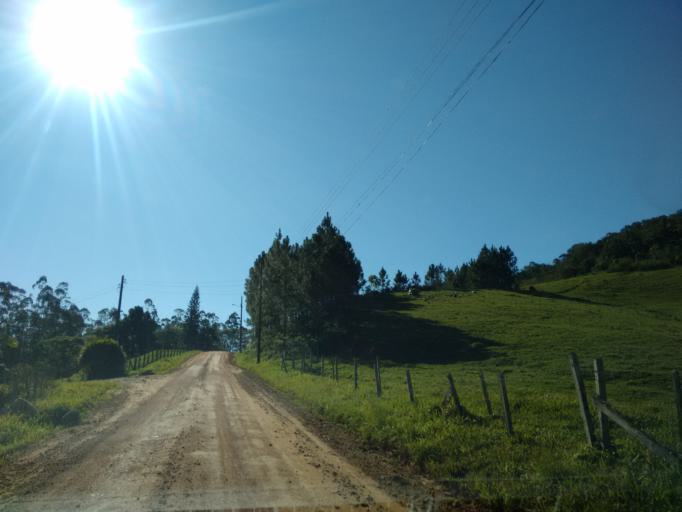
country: BR
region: Santa Catarina
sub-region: Pomerode
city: Pomerode
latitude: -26.6946
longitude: -49.1416
